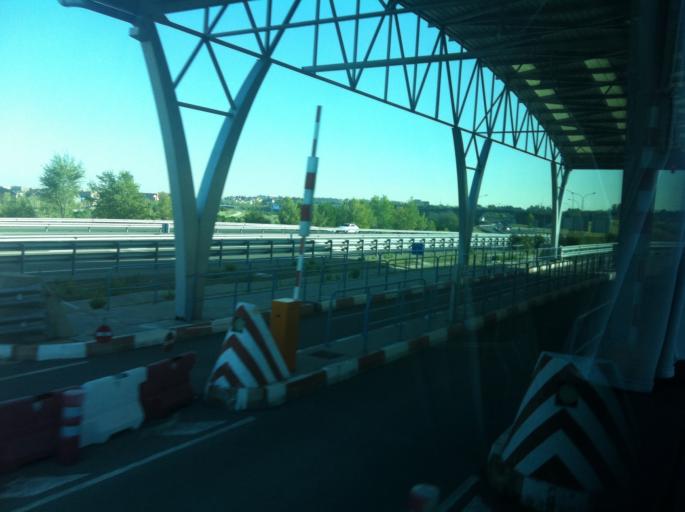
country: ES
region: Madrid
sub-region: Provincia de Madrid
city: Barajas de Madrid
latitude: 40.4746
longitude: -3.6016
